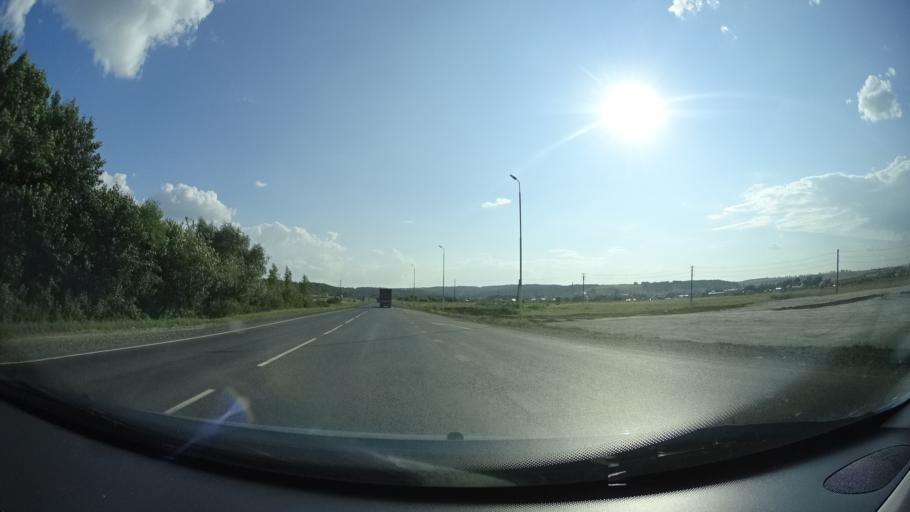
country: RU
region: Tatarstan
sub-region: Bavlinskiy Rayon
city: Bavly
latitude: 54.4658
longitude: 53.2949
